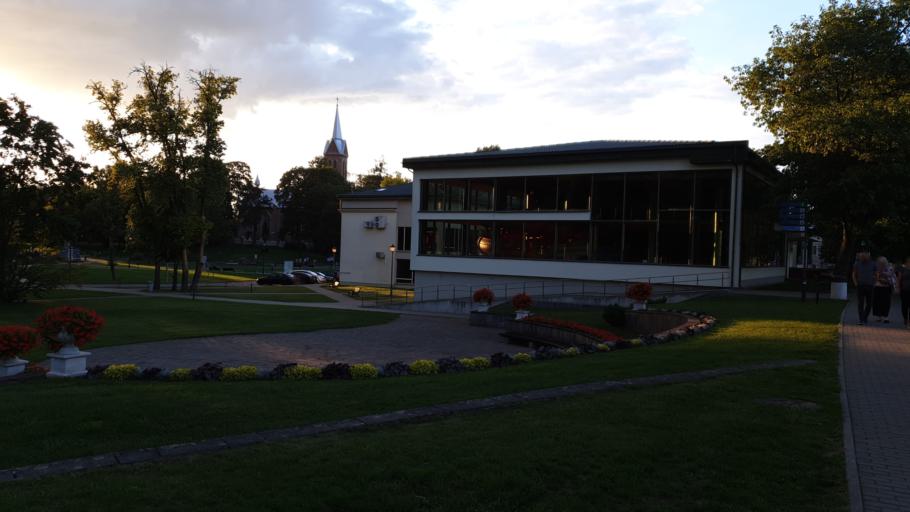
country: LT
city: Birstonas
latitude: 54.5997
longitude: 24.0358
